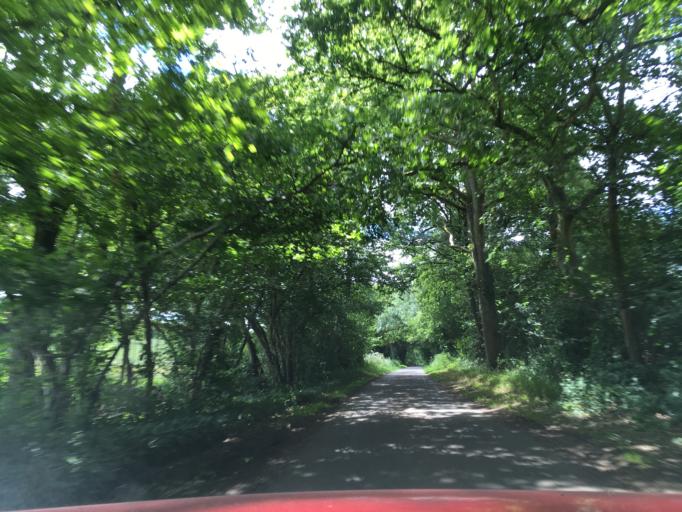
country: GB
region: England
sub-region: Hampshire
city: Highclere
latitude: 51.2828
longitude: -1.4167
